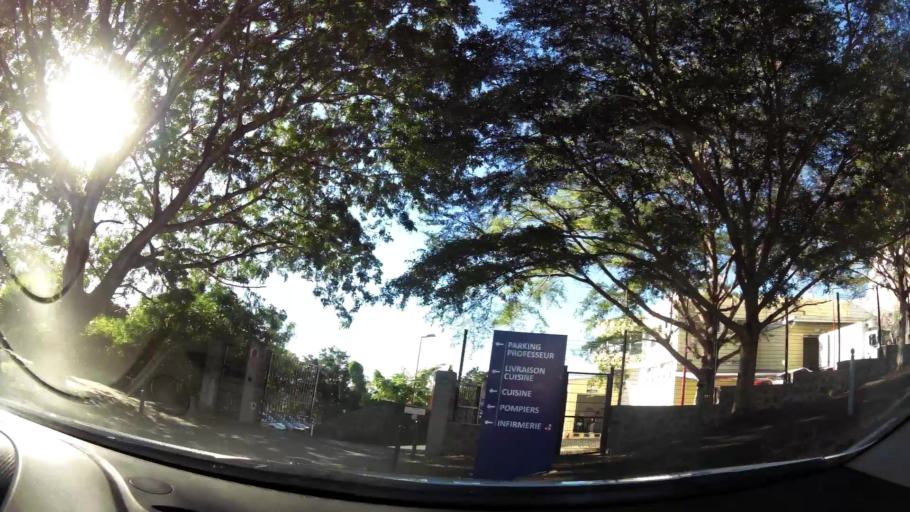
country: RE
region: Reunion
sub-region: Reunion
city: Saint-Denis
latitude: -20.8948
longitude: 55.4500
